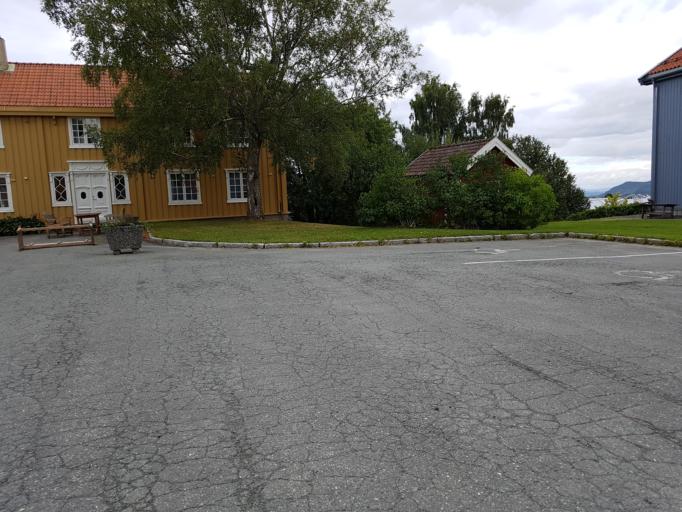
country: NO
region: Sor-Trondelag
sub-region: Trondheim
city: Trondheim
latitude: 63.4083
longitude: 10.4660
